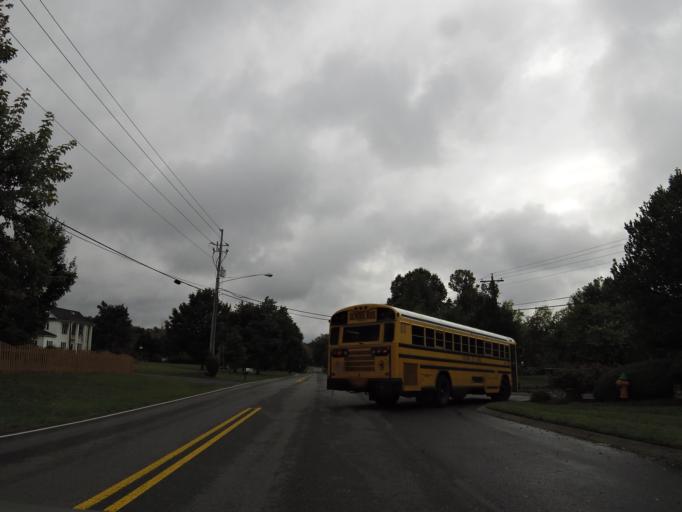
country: US
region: Tennessee
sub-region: Bradley County
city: Hopewell
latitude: 35.1992
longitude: -84.9075
